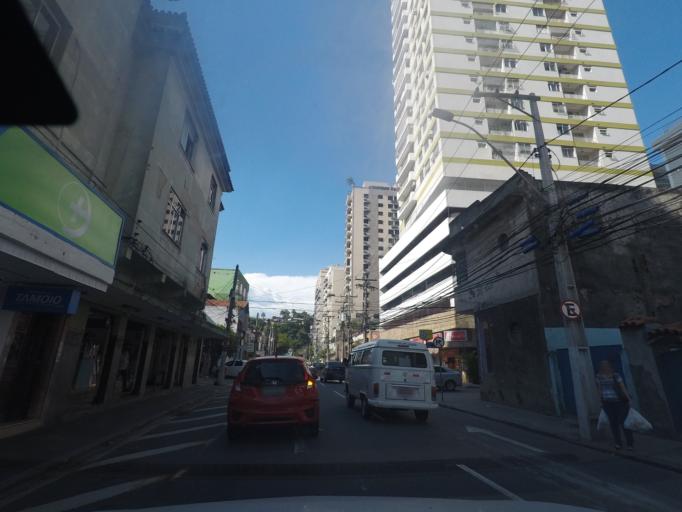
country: BR
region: Rio de Janeiro
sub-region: Niteroi
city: Niteroi
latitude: -22.9038
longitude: -43.1222
